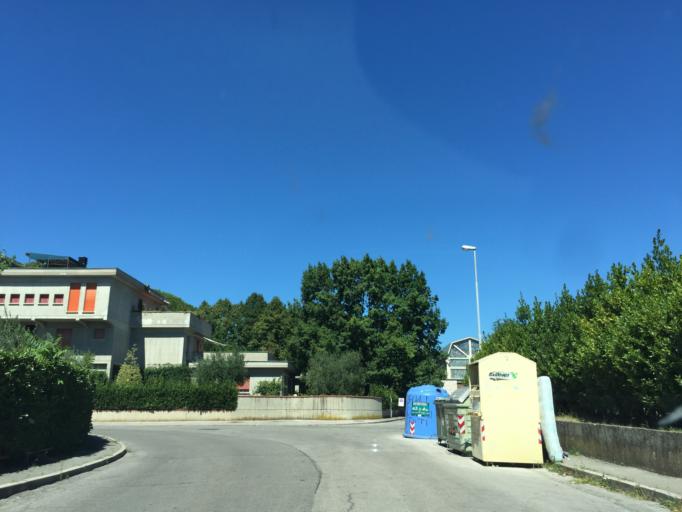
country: IT
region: Tuscany
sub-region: Provincia di Pistoia
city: Pistoia
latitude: 43.9477
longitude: 10.9072
